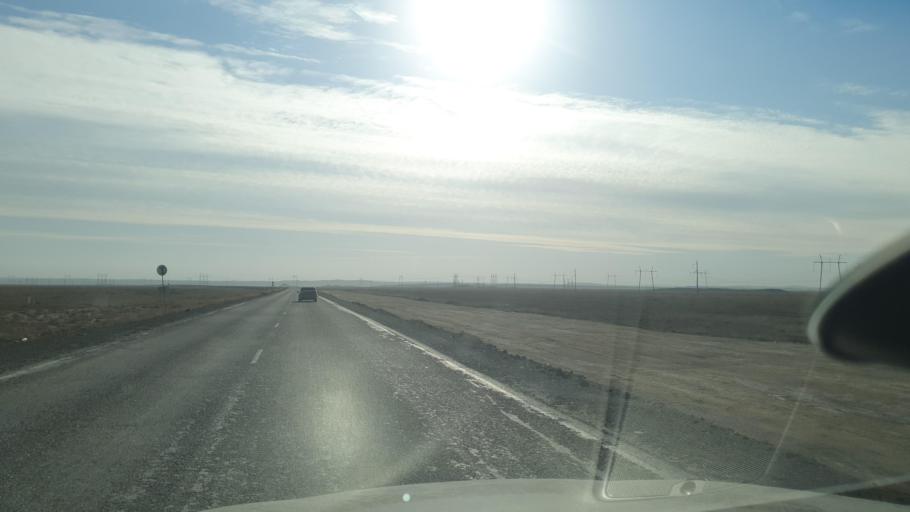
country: KZ
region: Zhambyl
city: Mynaral
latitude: 45.6196
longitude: 73.3961
